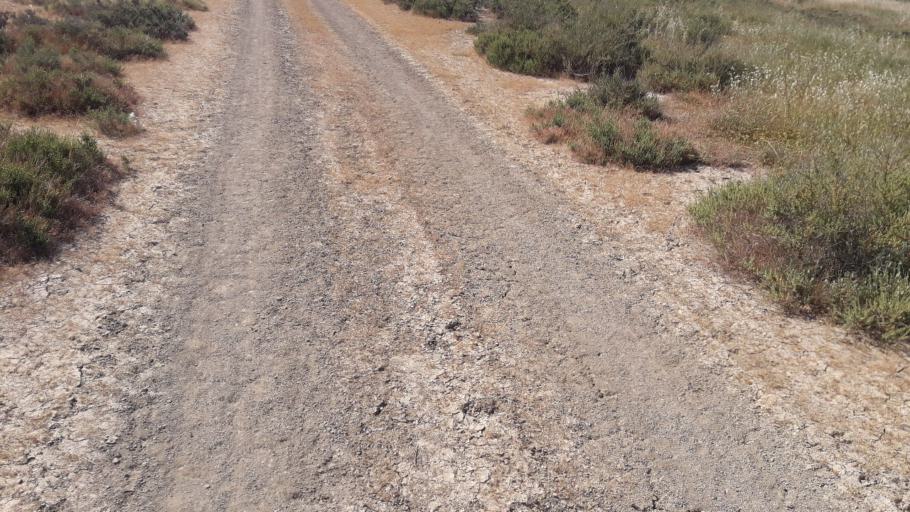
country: CY
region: Ammochostos
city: Famagusta
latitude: 35.1666
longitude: 33.8952
